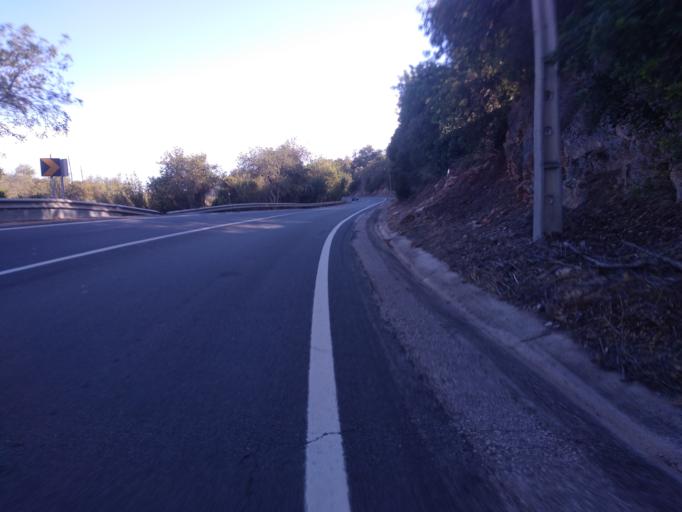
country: PT
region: Faro
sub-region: Sao Bras de Alportel
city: Sao Bras de Alportel
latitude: 37.1066
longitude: -7.9069
